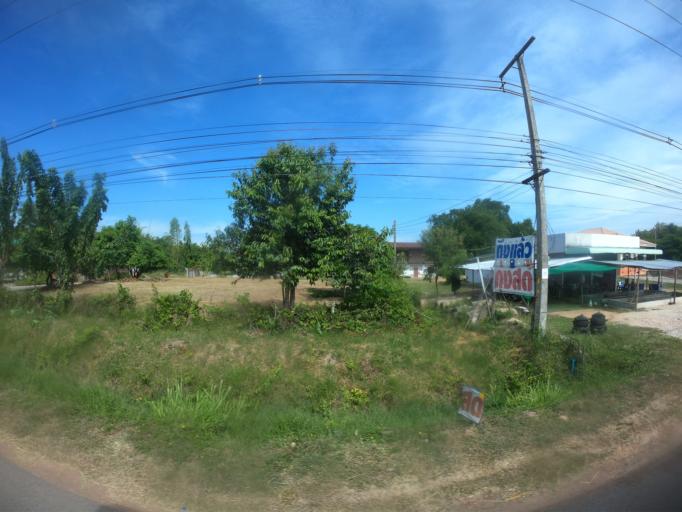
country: TH
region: Maha Sarakham
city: Chiang Yuen
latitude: 16.4433
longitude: 102.9955
